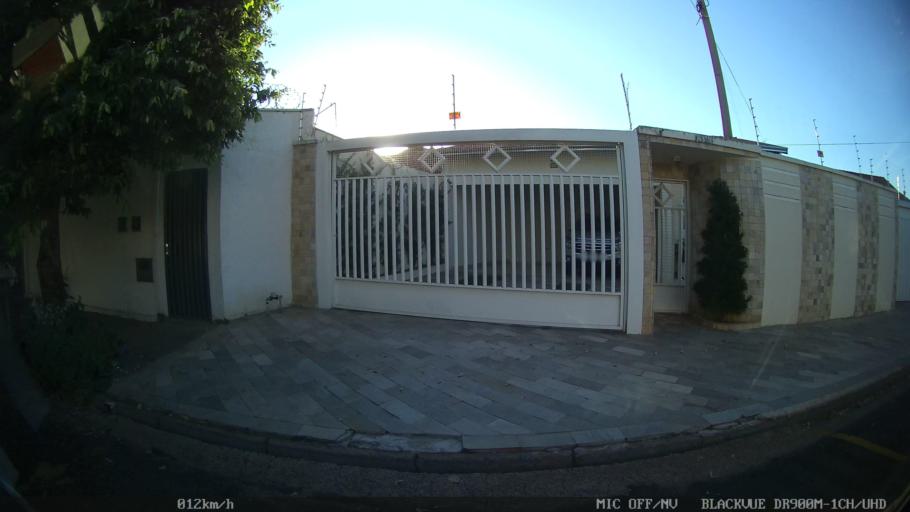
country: BR
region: Sao Paulo
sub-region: Sao Jose Do Rio Preto
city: Sao Jose do Rio Preto
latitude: -20.7904
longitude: -49.3628
